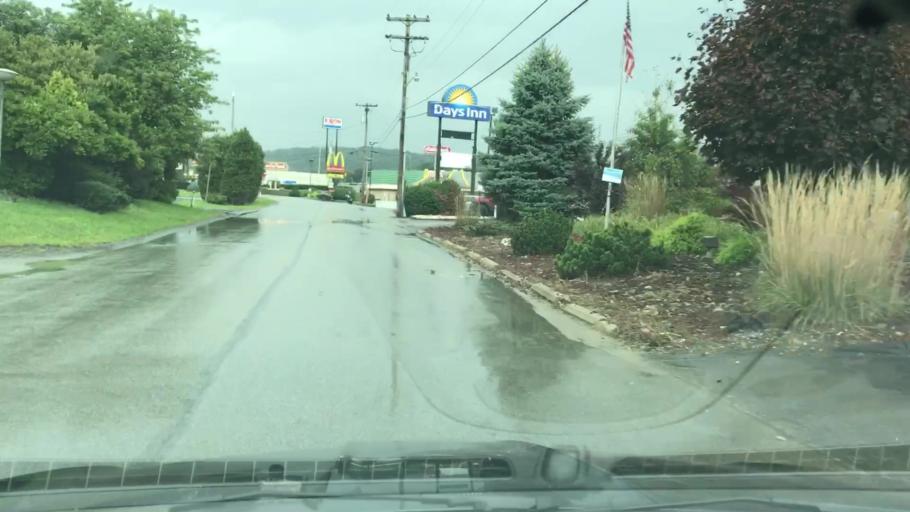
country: US
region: Pennsylvania
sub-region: Westmoreland County
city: New Stanton
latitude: 40.2180
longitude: -79.6118
